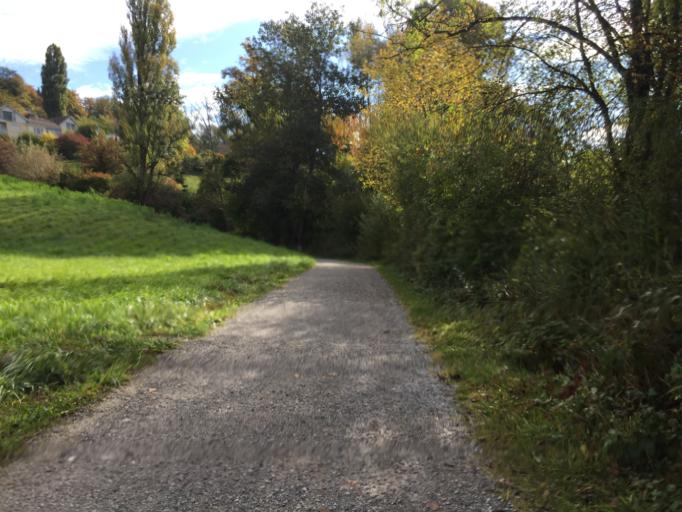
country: CH
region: Bern
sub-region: Bern-Mittelland District
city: Muri
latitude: 46.9219
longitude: 7.4957
